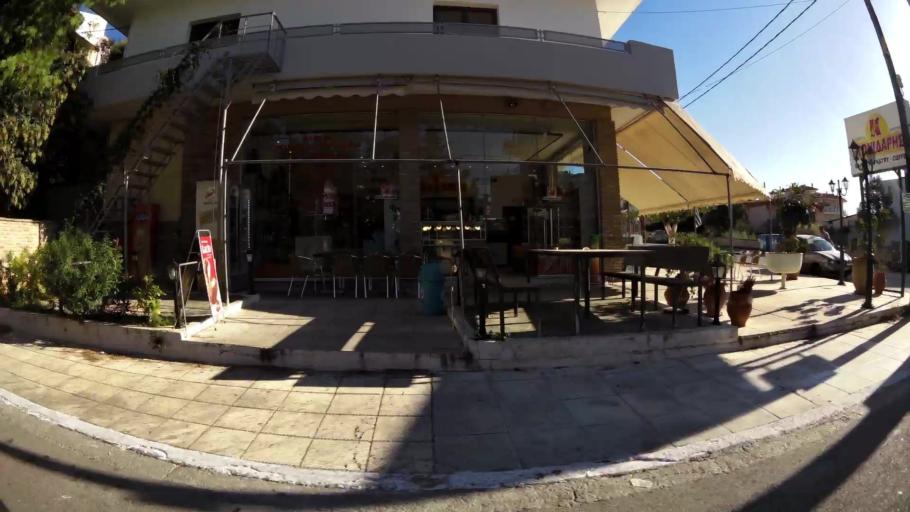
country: GR
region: Attica
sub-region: Nomarchia Anatolikis Attikis
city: Kalyvia Thorikou
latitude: 37.8383
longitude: 23.9235
